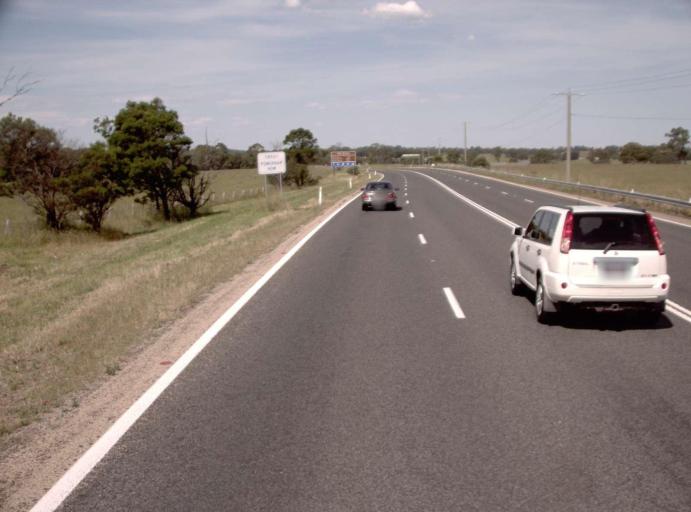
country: AU
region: Victoria
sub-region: East Gippsland
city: Bairnsdale
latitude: -37.8211
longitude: 147.7245
